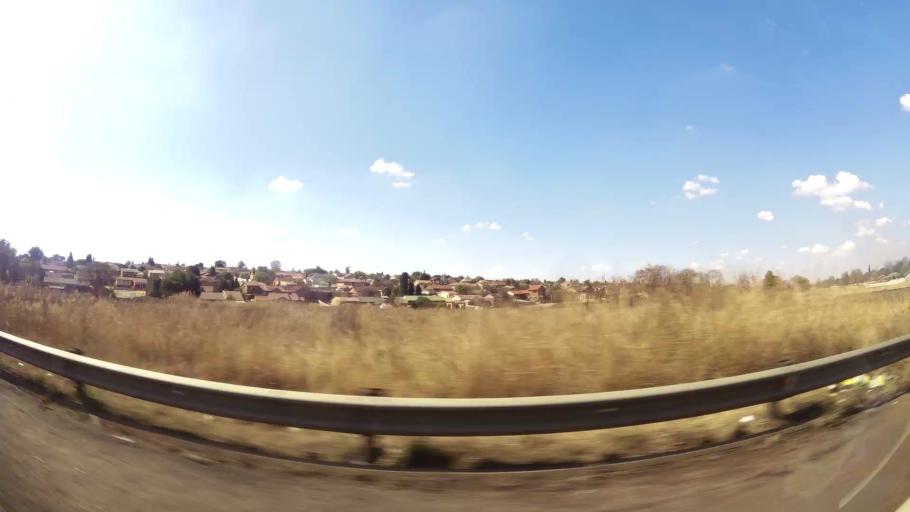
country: ZA
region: Mpumalanga
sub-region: Nkangala District Municipality
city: Witbank
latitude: -25.9318
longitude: 29.2369
